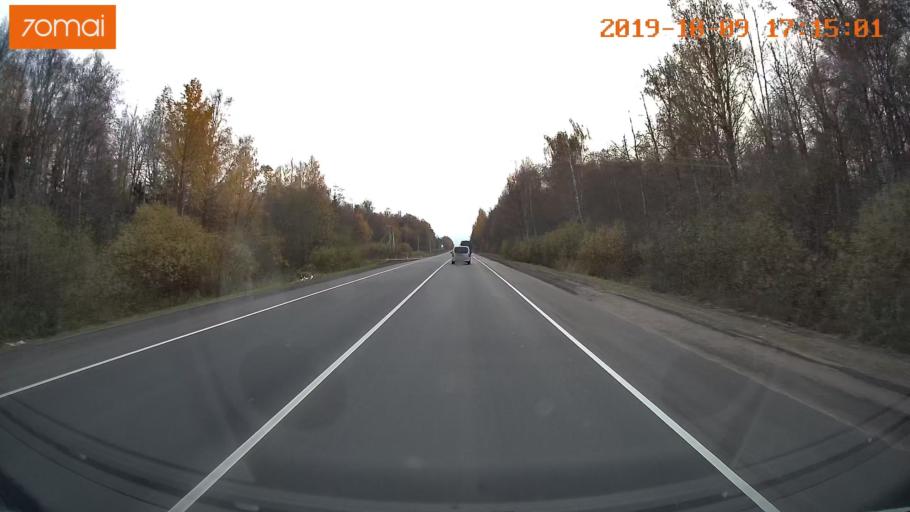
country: RU
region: Ivanovo
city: Furmanov
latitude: 57.3008
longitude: 41.1986
